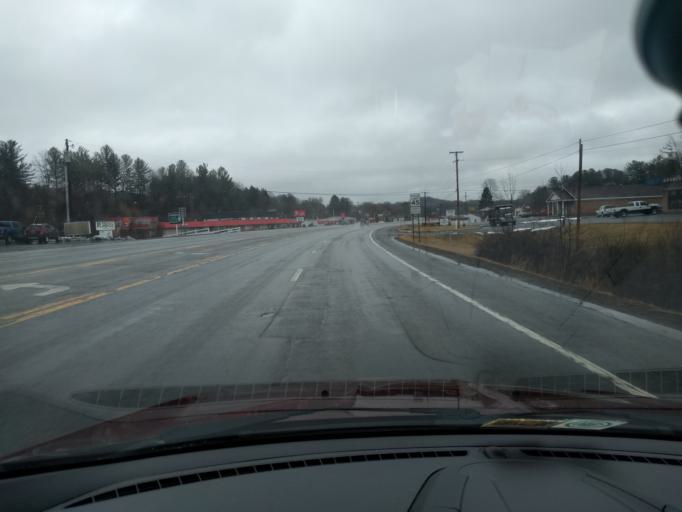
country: US
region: West Virginia
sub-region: Raleigh County
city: Crab Orchard
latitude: 37.7379
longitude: -81.2362
